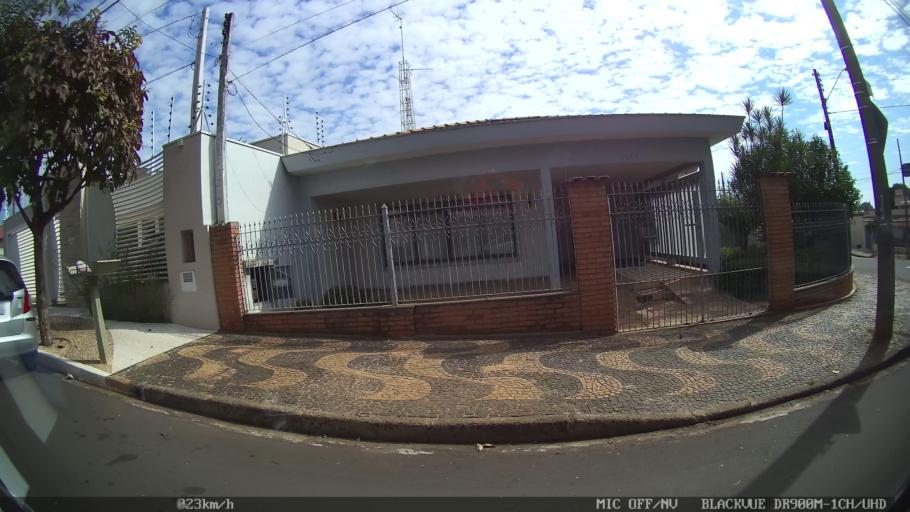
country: BR
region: Sao Paulo
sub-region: Santa Barbara D'Oeste
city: Santa Barbara d'Oeste
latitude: -22.7530
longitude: -47.4219
